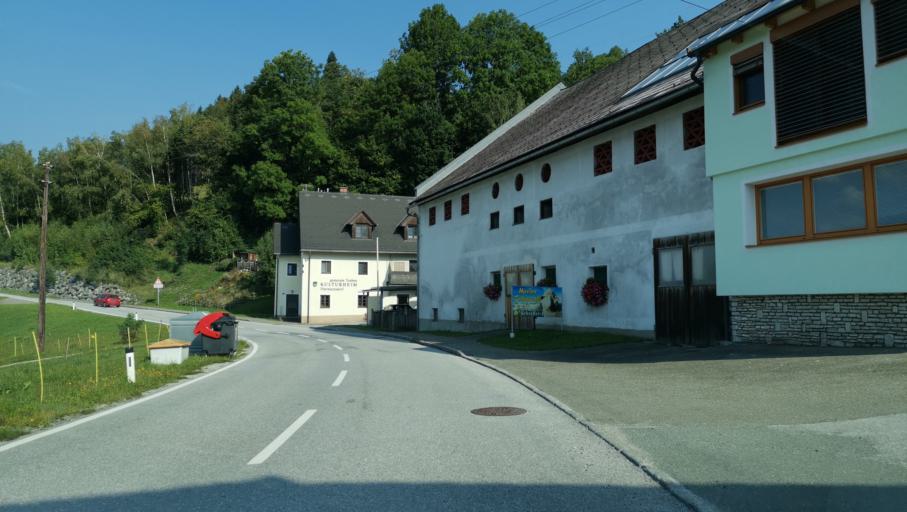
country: AT
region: Styria
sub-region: Politischer Bezirk Liezen
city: Trieben
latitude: 47.5043
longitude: 14.4766
